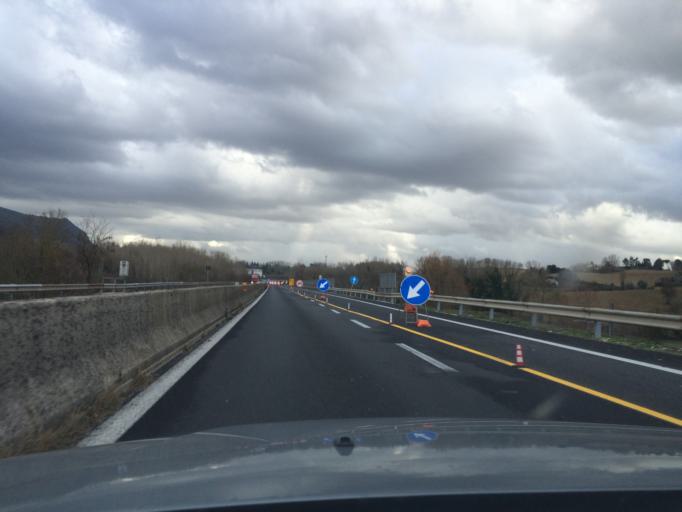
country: IT
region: Umbria
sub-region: Provincia di Terni
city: San Gemini
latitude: 42.6418
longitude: 12.5410
